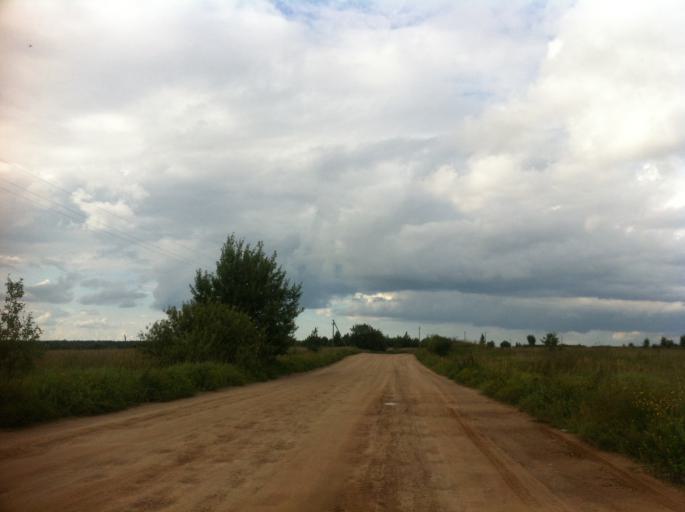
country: RU
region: Pskov
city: Izborsk
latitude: 57.8188
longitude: 27.9782
